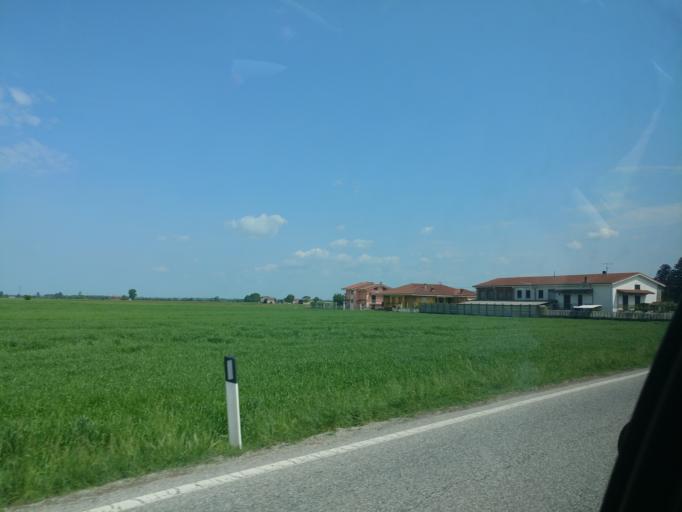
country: IT
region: Piedmont
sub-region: Provincia di Torino
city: Cavour
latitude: 44.7518
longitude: 7.4057
